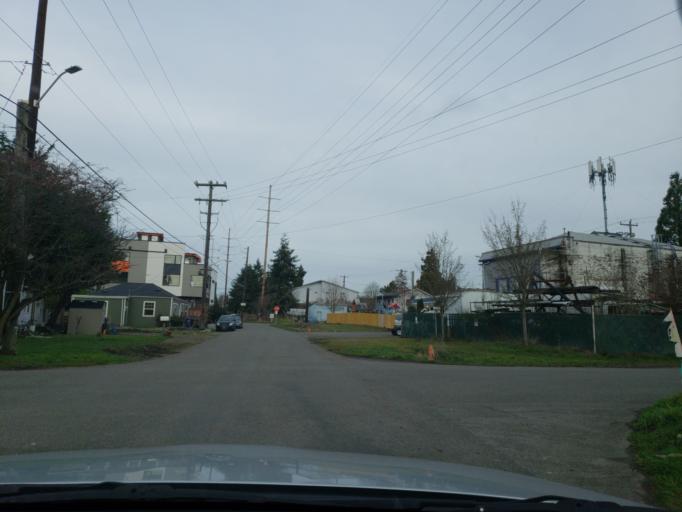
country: US
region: Washington
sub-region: King County
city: Shoreline
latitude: 47.7028
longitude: -122.3509
